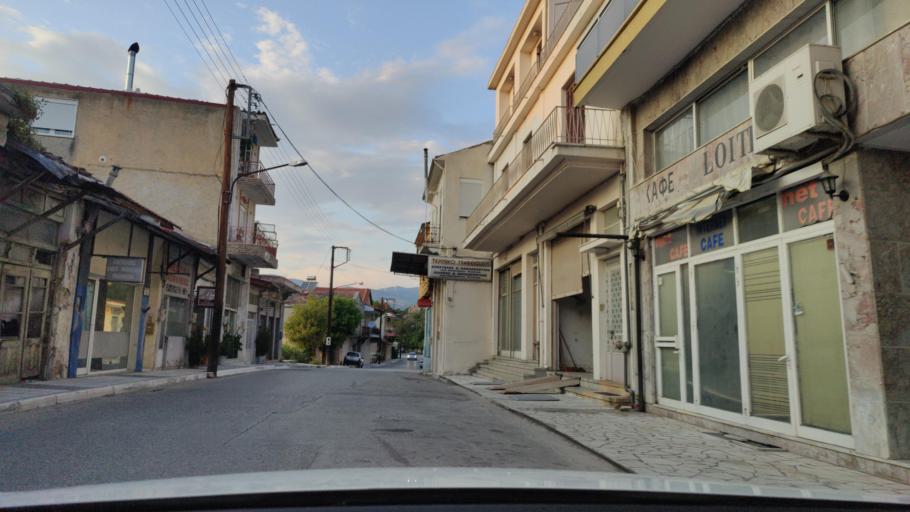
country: GR
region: Central Macedonia
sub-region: Nomos Serron
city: Sidirokastro
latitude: 41.2380
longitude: 23.3945
